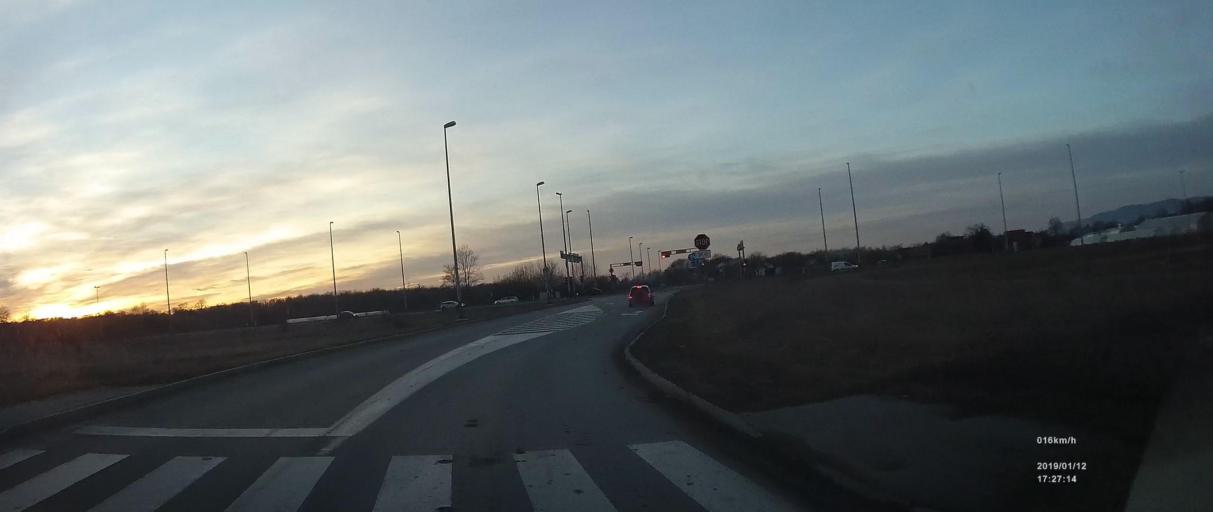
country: HR
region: Zagrebacka
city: Micevec
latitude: 45.7409
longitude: 16.1071
